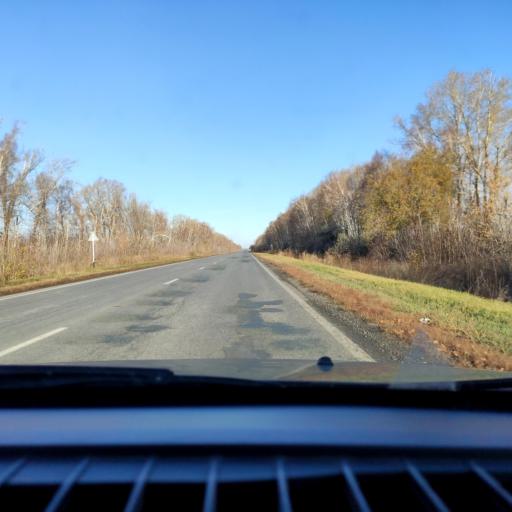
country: RU
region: Samara
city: Tol'yatti
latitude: 53.6079
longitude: 49.3180
